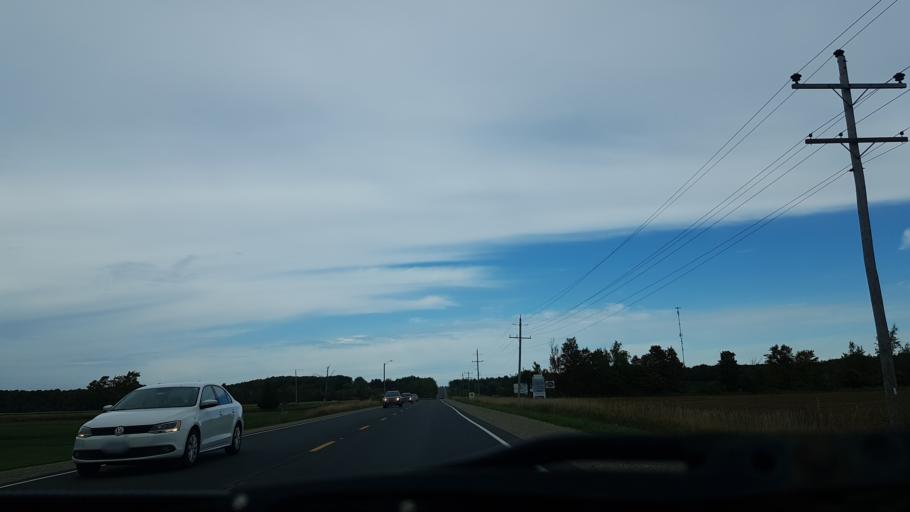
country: CA
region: Ontario
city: Angus
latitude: 44.3186
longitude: -80.0742
